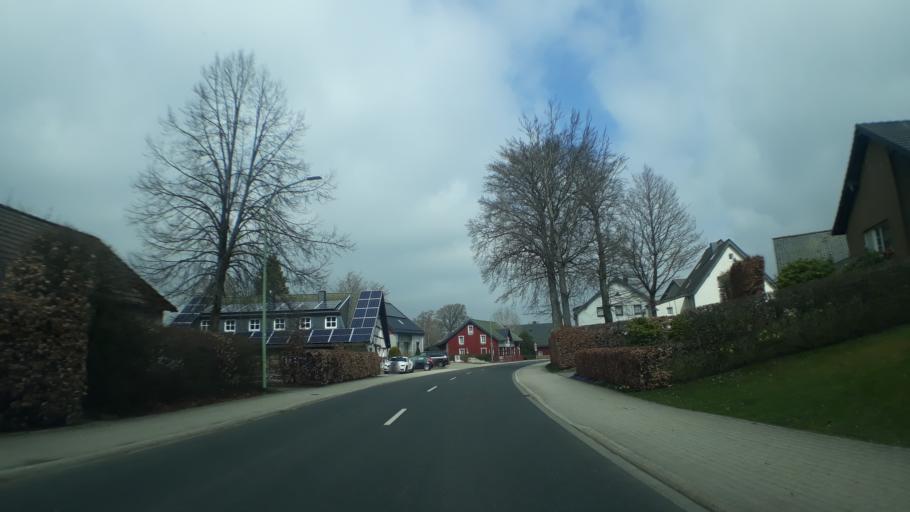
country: DE
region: North Rhine-Westphalia
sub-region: Regierungsbezirk Koln
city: Monschau
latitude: 50.5182
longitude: 6.2185
